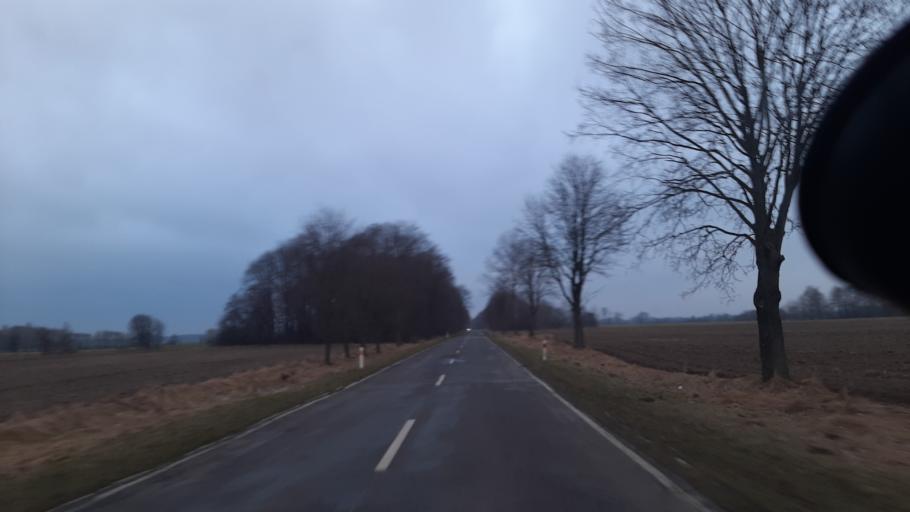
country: PL
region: Lublin Voivodeship
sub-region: Powiat parczewski
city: Sosnowica
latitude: 51.6153
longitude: 23.1128
